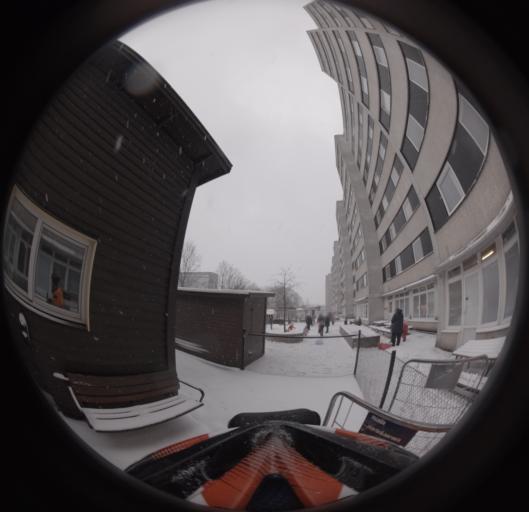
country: SE
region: Stockholm
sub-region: Sollentuna Kommun
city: Sollentuna
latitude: 59.4275
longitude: 17.9453
